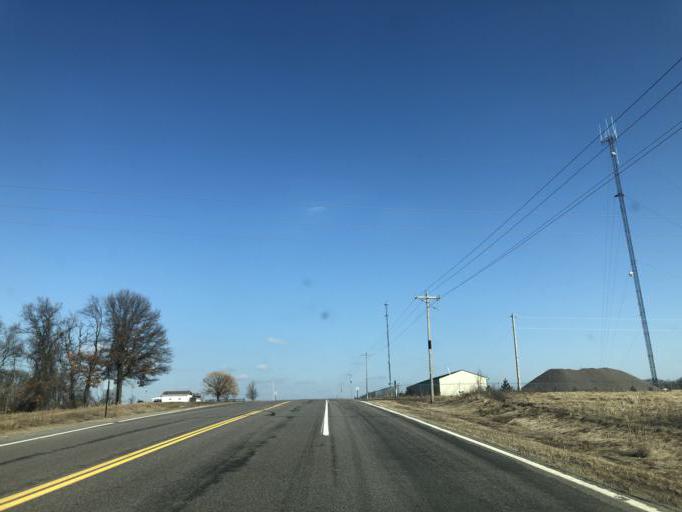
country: US
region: Minnesota
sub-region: Sherburne County
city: Becker
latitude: 45.4296
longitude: -93.8411
